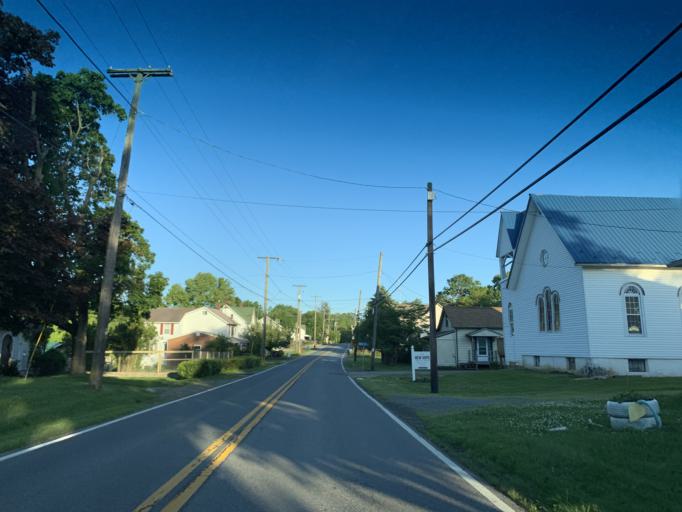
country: US
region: Maryland
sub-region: Cecil County
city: Elkton
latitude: 39.6599
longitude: -75.8278
